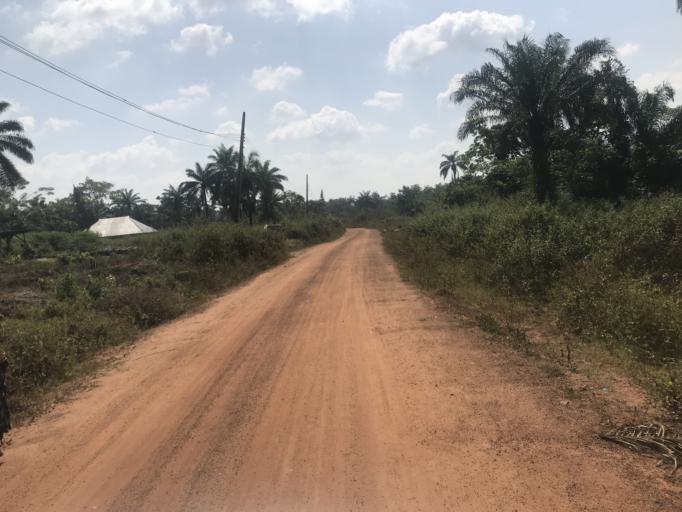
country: NG
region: Osun
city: Iragbiji
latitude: 7.8822
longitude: 4.7007
